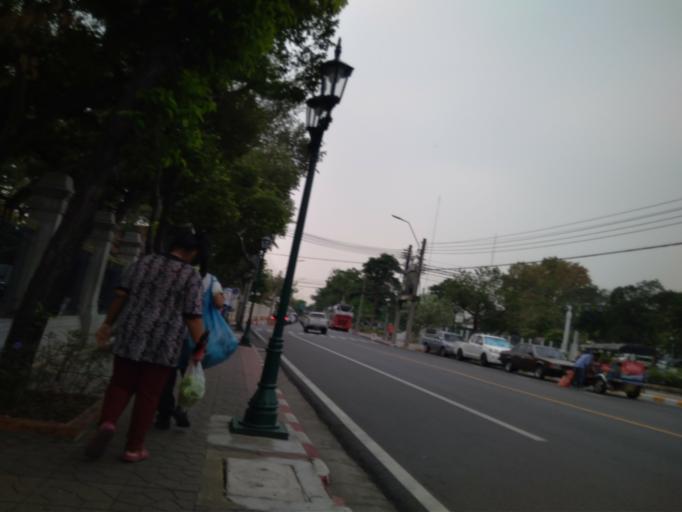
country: TH
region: Bangkok
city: Bangkok
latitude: 13.7502
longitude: 100.4966
